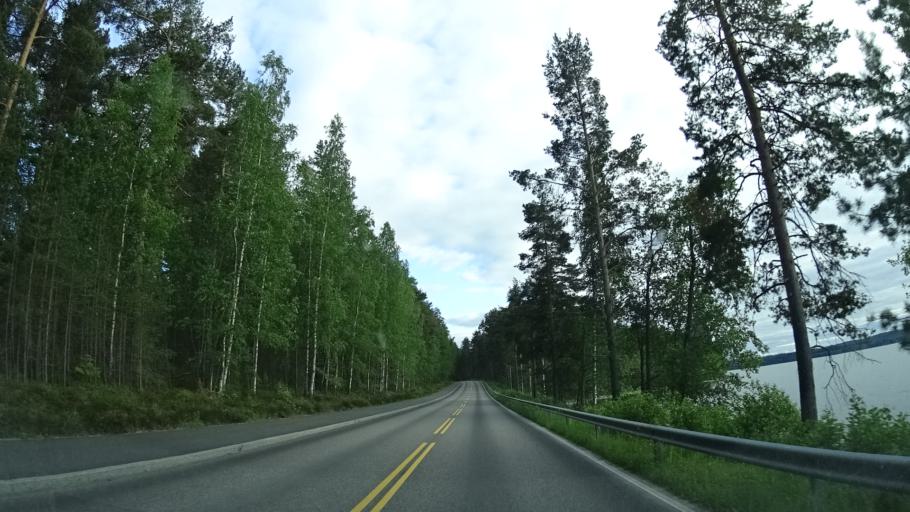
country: FI
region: Paijanne Tavastia
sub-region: Lahti
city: Asikkala
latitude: 61.2843
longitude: 25.5305
